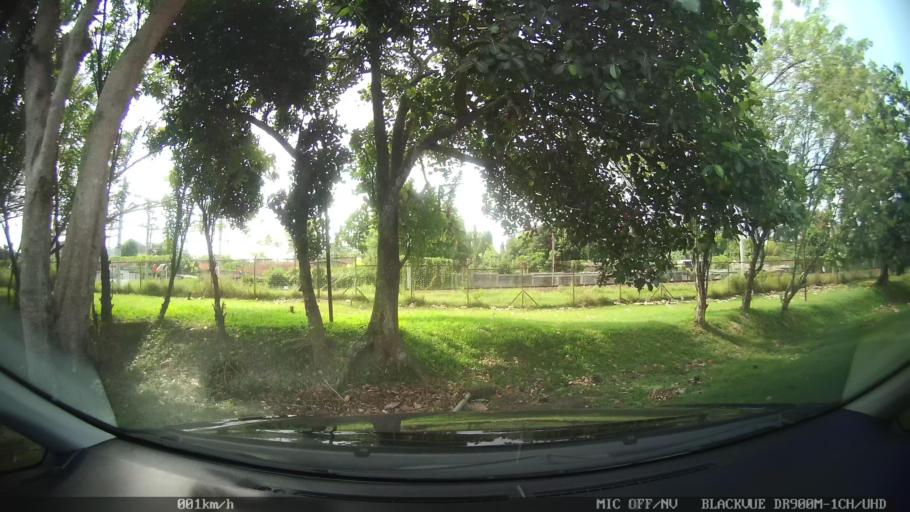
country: ID
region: Daerah Istimewa Yogyakarta
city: Depok
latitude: -7.7856
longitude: 110.4337
